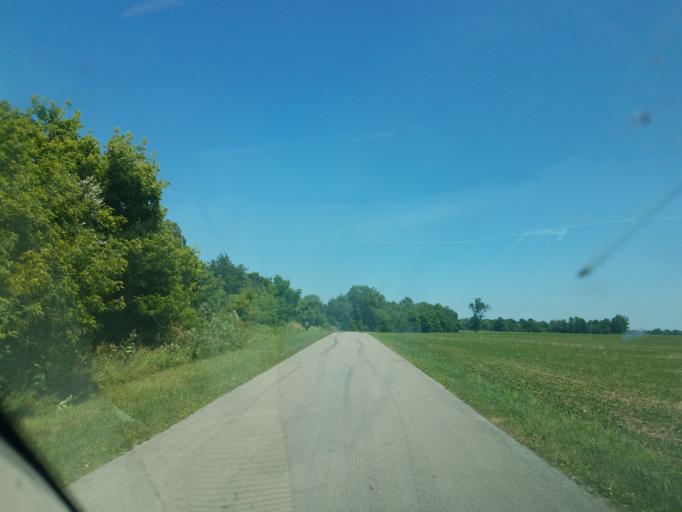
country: US
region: Ohio
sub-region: Hardin County
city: Forest
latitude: 40.8001
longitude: -83.5340
